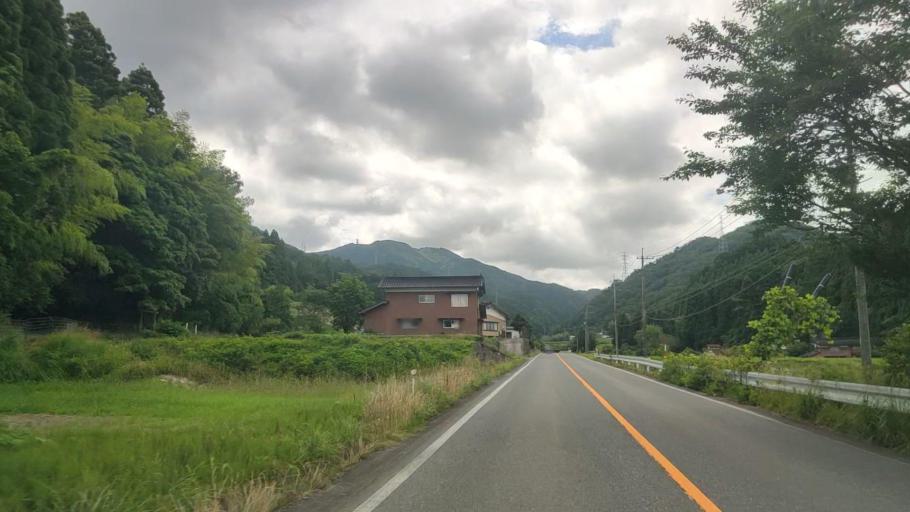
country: JP
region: Tottori
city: Yonago
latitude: 35.2918
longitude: 133.4208
